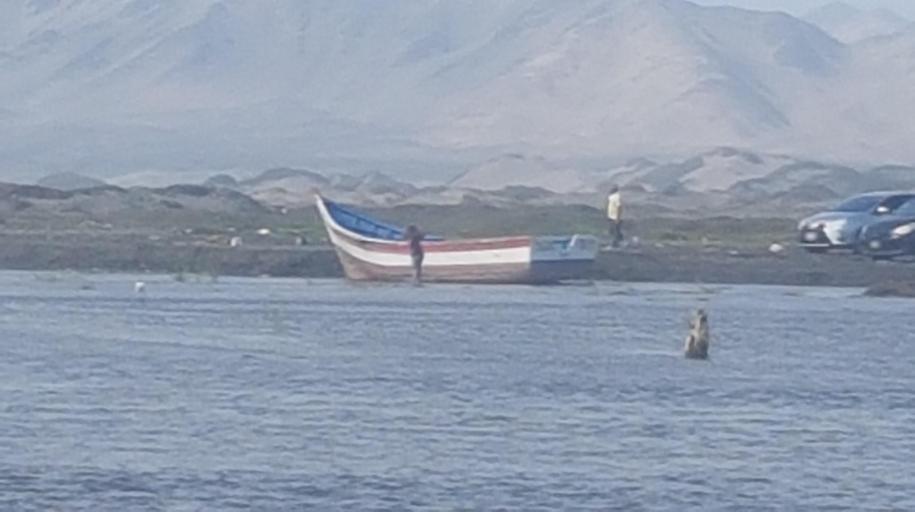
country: PE
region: La Libertad
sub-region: Viru
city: Chao
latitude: -8.6197
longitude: -78.7539
